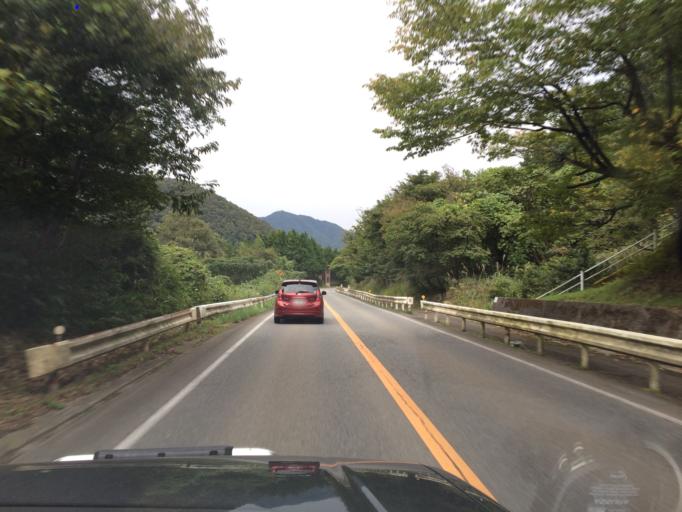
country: JP
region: Hyogo
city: Toyooka
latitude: 35.4116
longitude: 134.7829
